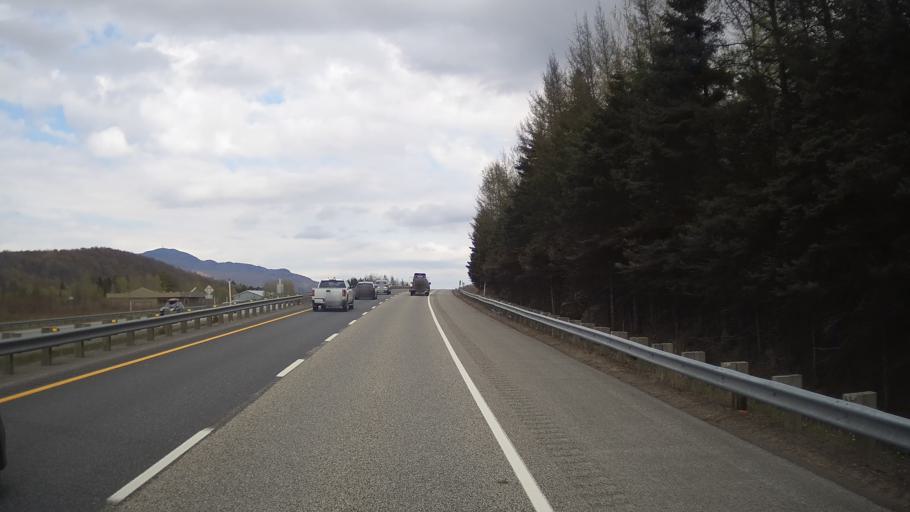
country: CA
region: Quebec
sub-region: Monteregie
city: Waterloo
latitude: 45.3049
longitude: -72.3447
